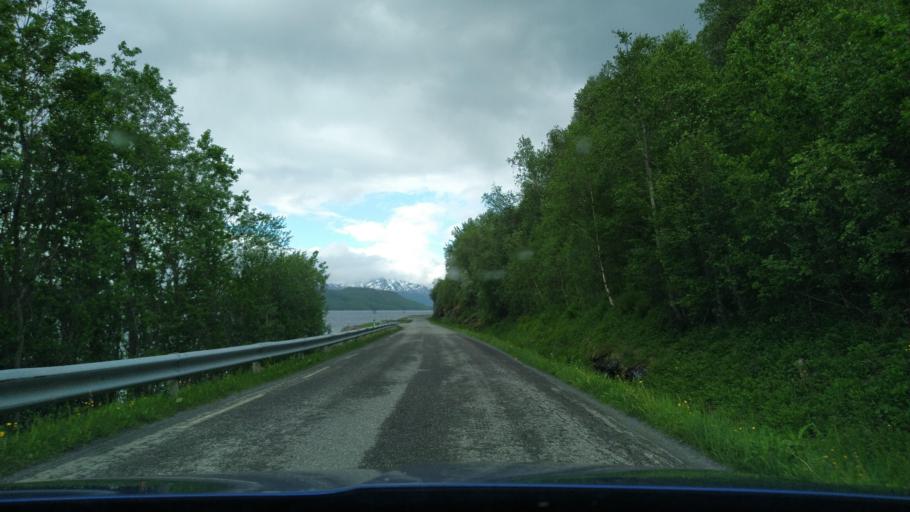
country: NO
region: Troms
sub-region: Lenvik
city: Finnsnes
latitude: 69.1372
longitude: 17.9052
